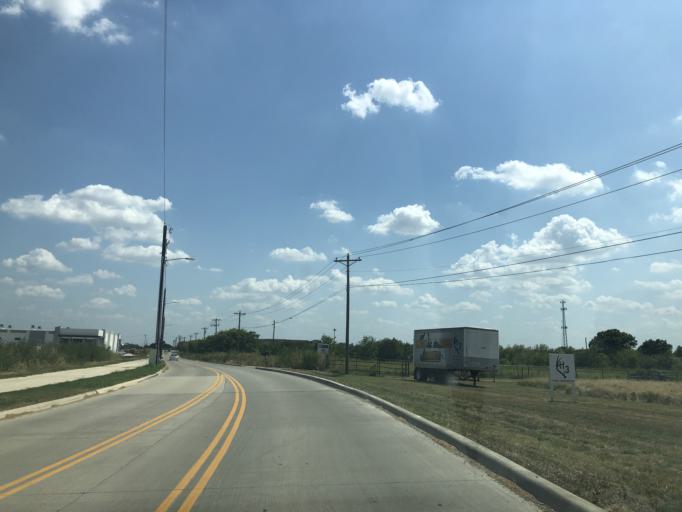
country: US
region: Texas
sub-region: Tarrant County
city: Haslet
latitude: 32.9384
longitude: -97.3229
